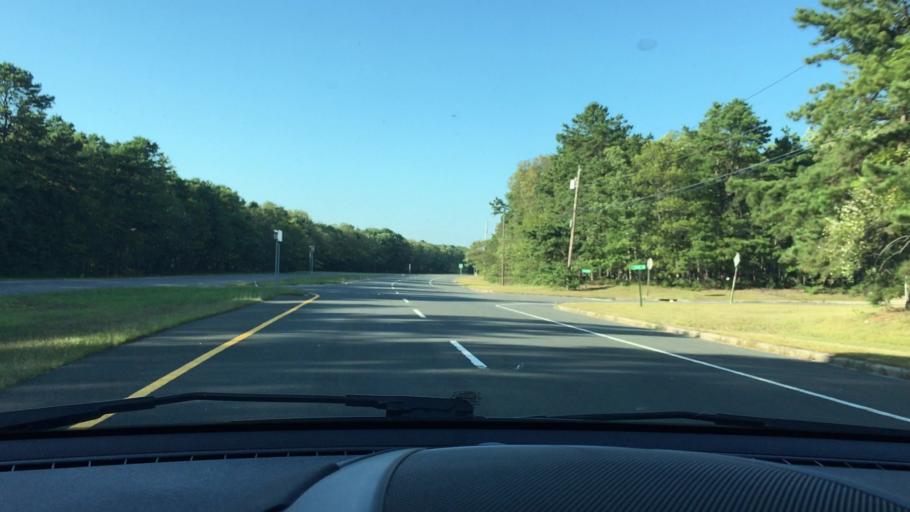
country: US
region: New York
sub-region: Suffolk County
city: Ridge
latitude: 40.9011
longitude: -72.8828
